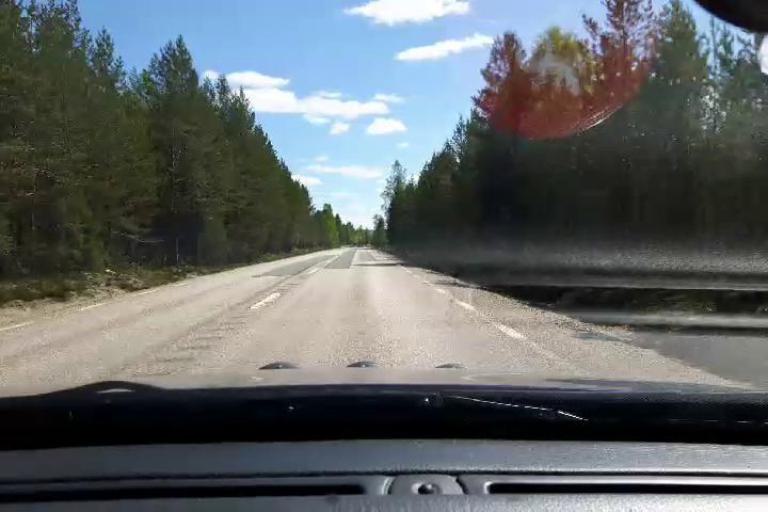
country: SE
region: Gaevleborg
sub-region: Ljusdals Kommun
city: Farila
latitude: 61.9700
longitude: 15.3483
